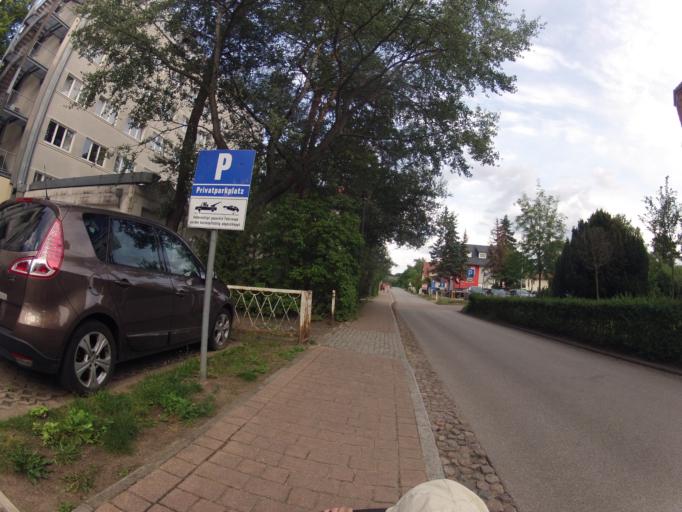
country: DE
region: Mecklenburg-Vorpommern
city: Seebad Heringsdorf
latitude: 53.9379
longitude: 14.1972
